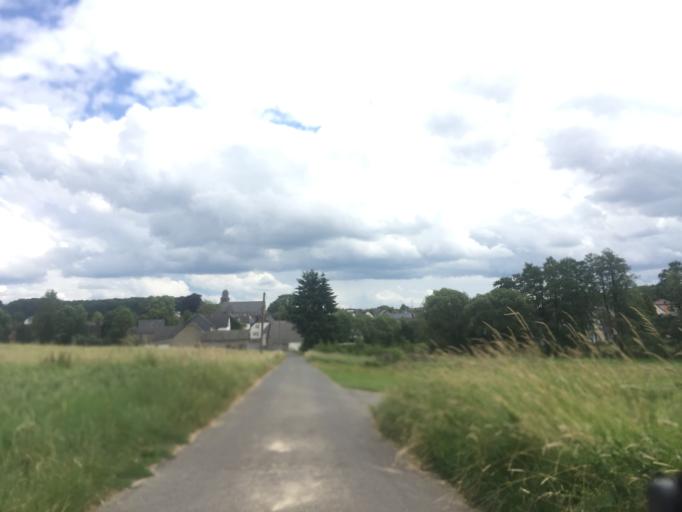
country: DE
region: Rheinland-Pfalz
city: Steinefrenz
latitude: 50.4602
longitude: 7.9277
